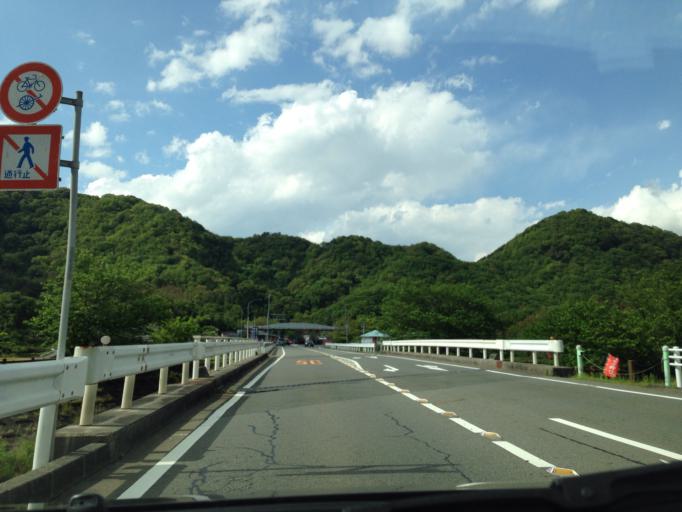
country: JP
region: Shizuoka
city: Mishima
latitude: 35.0560
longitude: 138.9237
